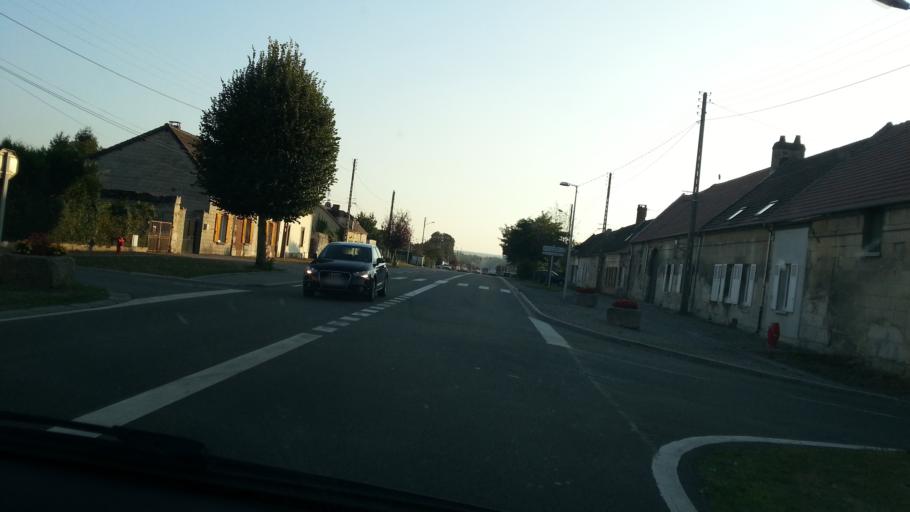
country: FR
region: Picardie
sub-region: Departement de l'Oise
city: Saint-Martin-Longueau
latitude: 49.3451
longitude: 2.6073
